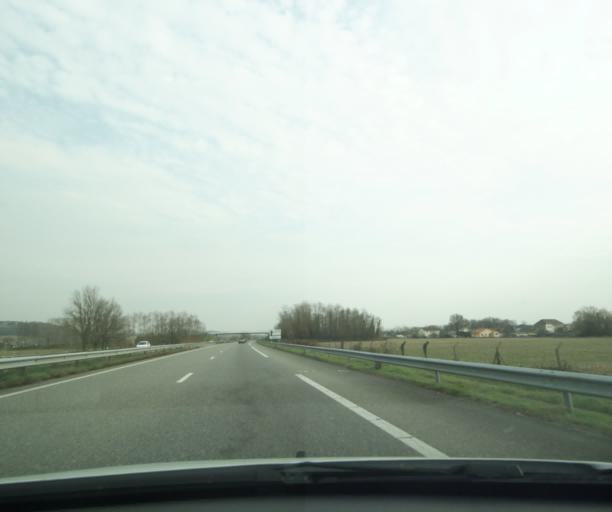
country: FR
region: Aquitaine
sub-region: Departement des Pyrenees-Atlantiques
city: Artix
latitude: 43.4125
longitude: -0.5695
